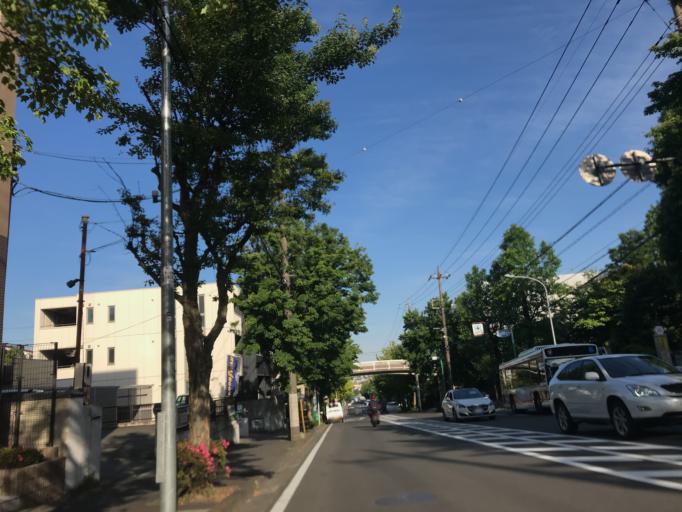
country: JP
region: Tokyo
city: Chofugaoka
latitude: 35.5707
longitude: 139.5418
